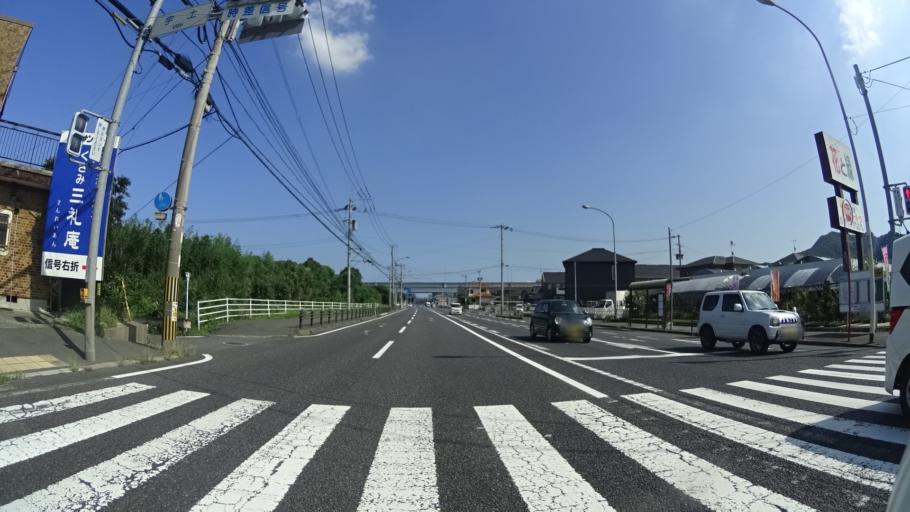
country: JP
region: Fukuoka
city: Kanda
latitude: 33.8009
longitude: 130.9684
